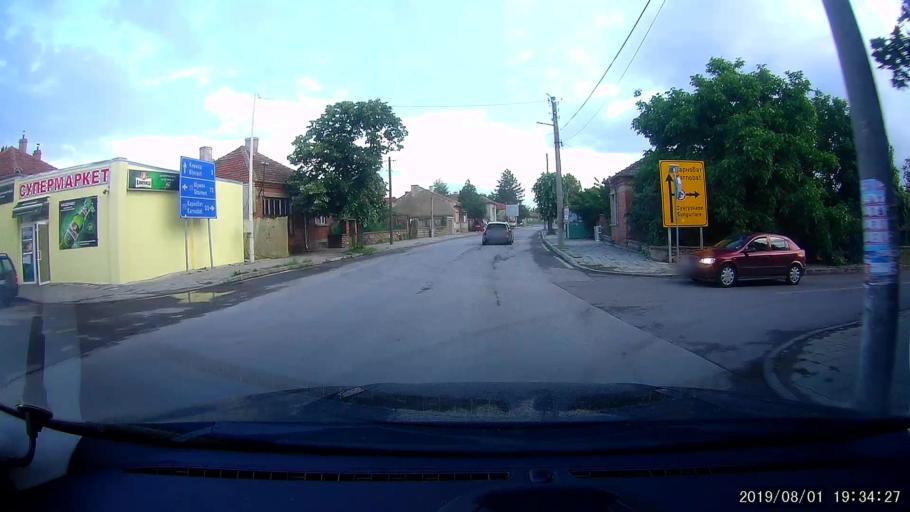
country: BG
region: Burgas
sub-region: Obshtina Sungurlare
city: Sungurlare
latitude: 42.7710
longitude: 26.8780
